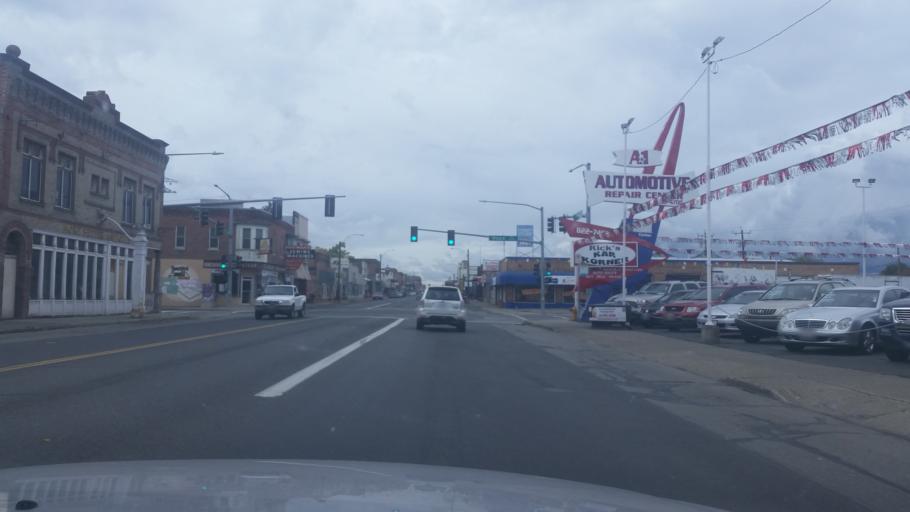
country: US
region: Washington
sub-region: Spokane County
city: Spokane
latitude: 47.6573
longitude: -117.3805
